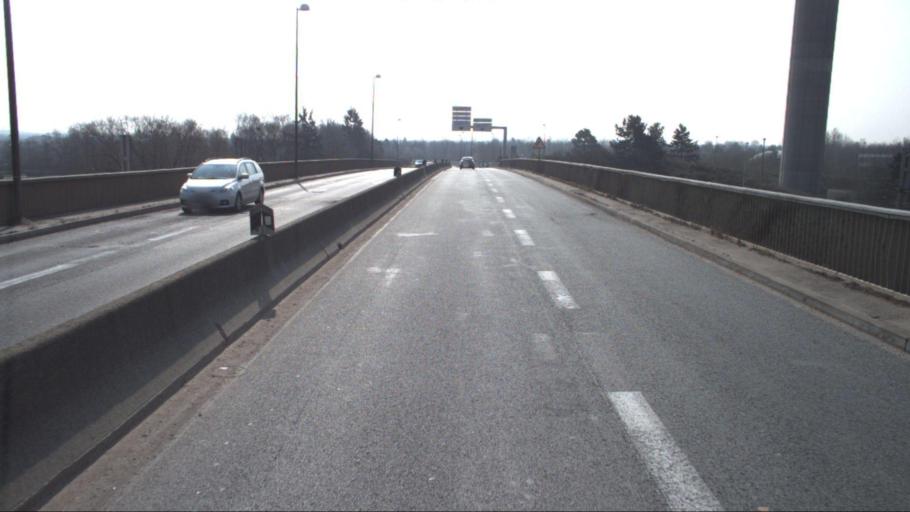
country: FR
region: Ile-de-France
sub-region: Departement des Yvelines
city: Trappes
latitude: 48.7809
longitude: 2.0265
